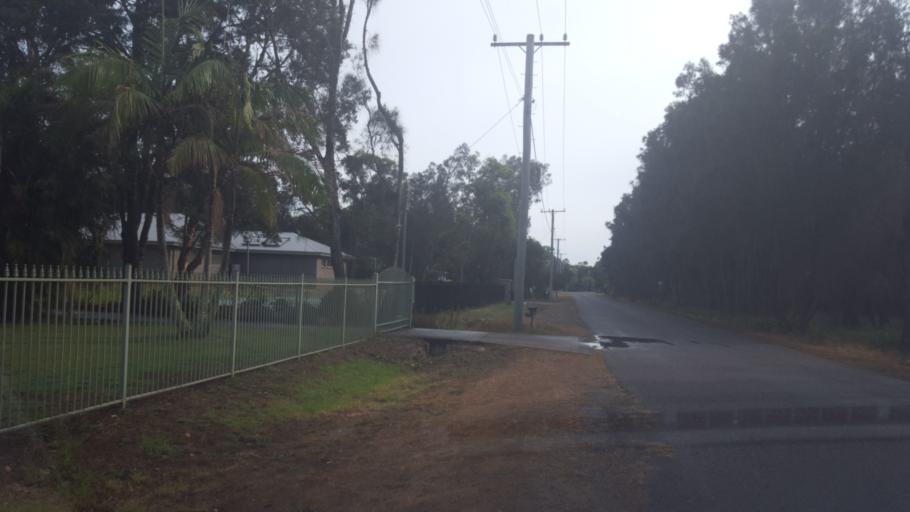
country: AU
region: New South Wales
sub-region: Port Stephens Shire
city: Anna Bay
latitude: -32.7705
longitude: 152.1137
